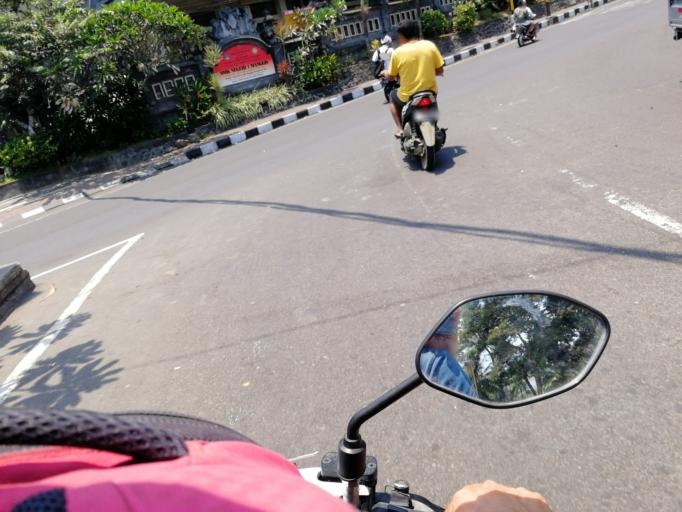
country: ID
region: Bali
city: Padangbai
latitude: -8.5202
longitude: 115.4978
